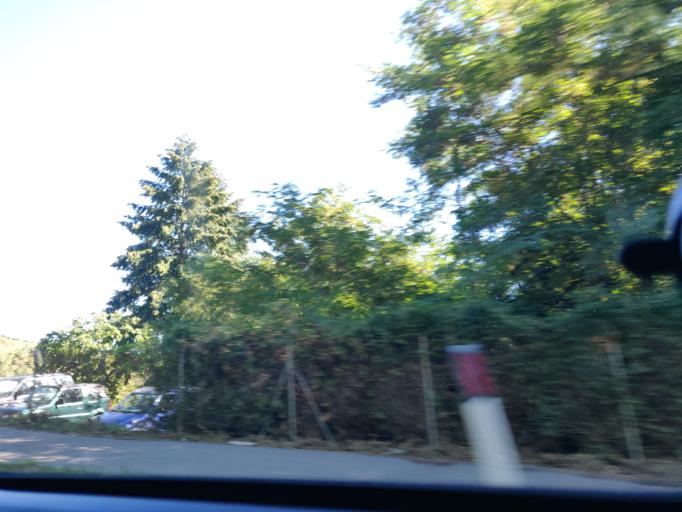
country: IT
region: Tuscany
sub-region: Provincia di Siena
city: Piancastagnaio
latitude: 42.8612
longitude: 11.6778
